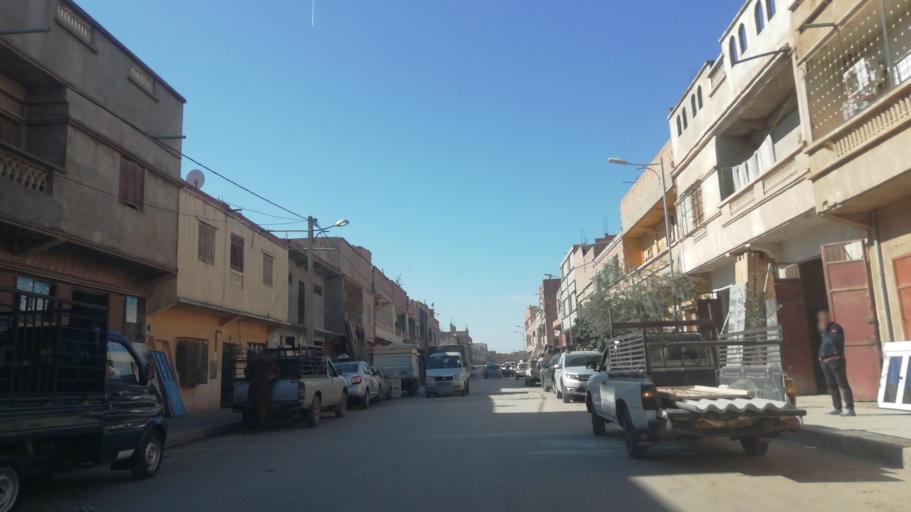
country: DZ
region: Oran
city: Sidi ech Chahmi
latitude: 35.6465
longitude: -0.5719
